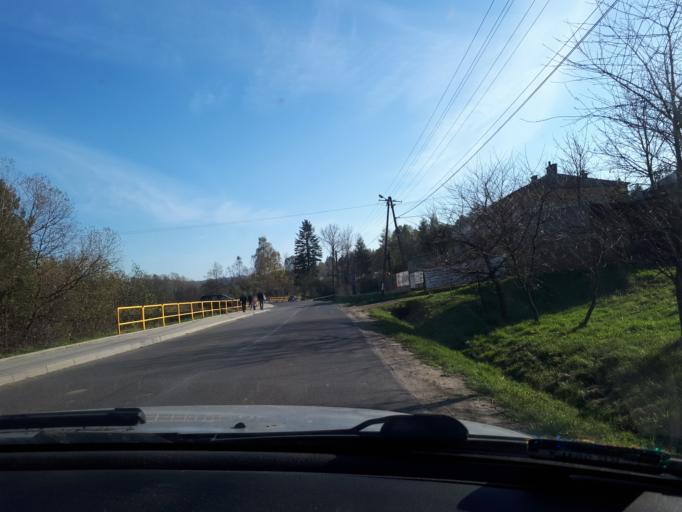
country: PL
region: Subcarpathian Voivodeship
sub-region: Powiat debicki
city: Debica
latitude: 49.9956
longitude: 21.4194
